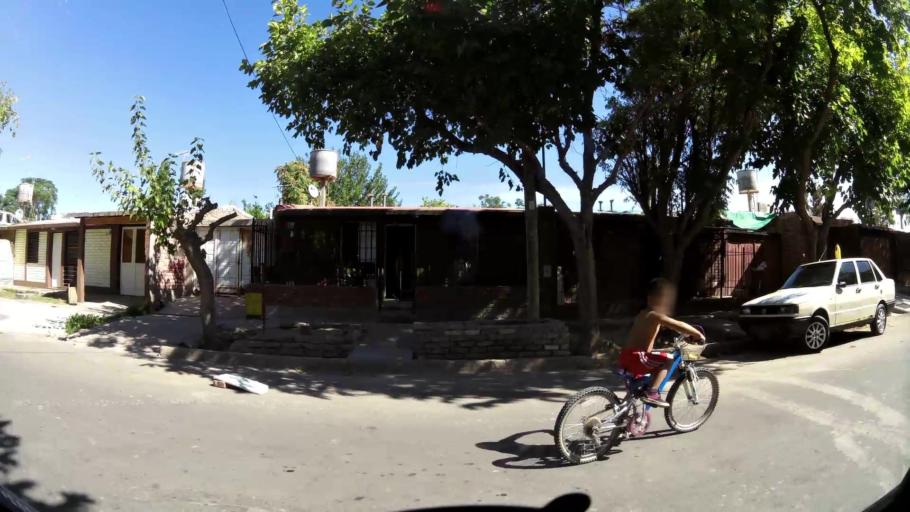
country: AR
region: Mendoza
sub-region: Departamento de Godoy Cruz
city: Godoy Cruz
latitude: -32.9525
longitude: -68.8230
